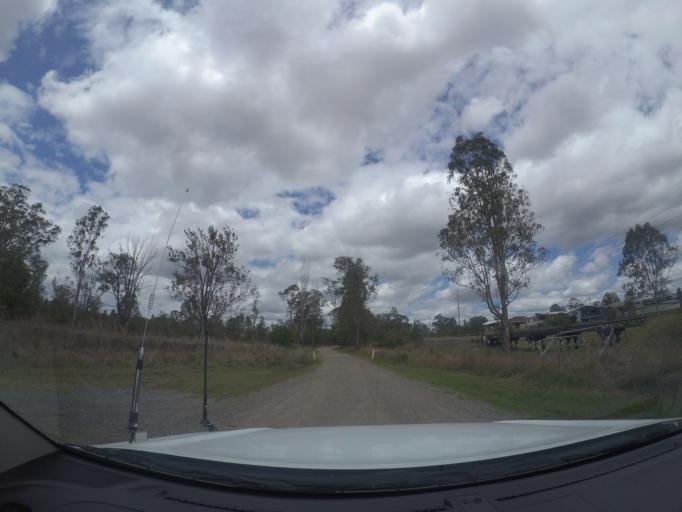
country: AU
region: Queensland
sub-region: Logan
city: Cedar Vale
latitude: -27.8289
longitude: 153.0370
